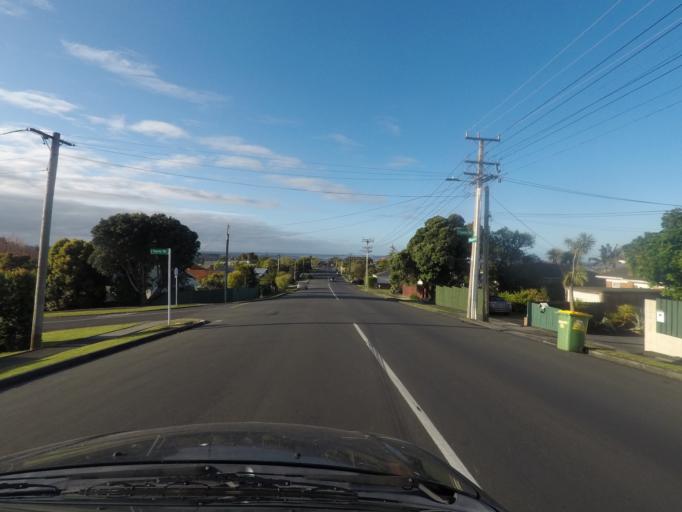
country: NZ
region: Auckland
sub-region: Auckland
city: Waitakere
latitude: -36.9163
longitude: 174.6579
